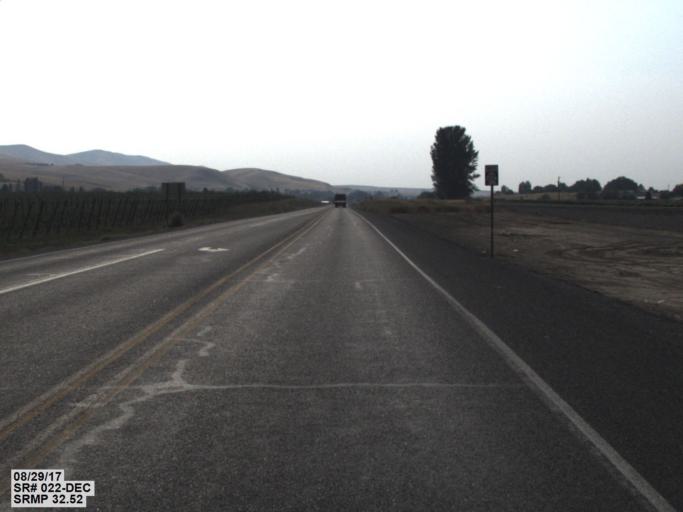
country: US
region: Washington
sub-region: Benton County
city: Prosser
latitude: 46.1926
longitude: -119.8100
